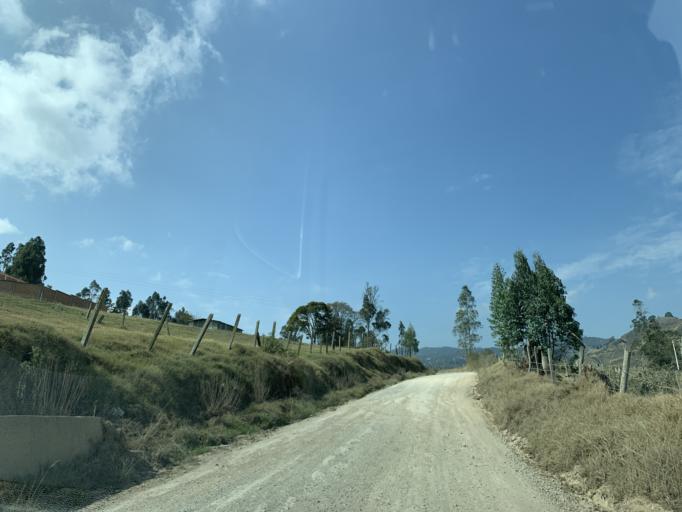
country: CO
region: Boyaca
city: Turmeque
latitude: 5.3081
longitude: -73.4986
